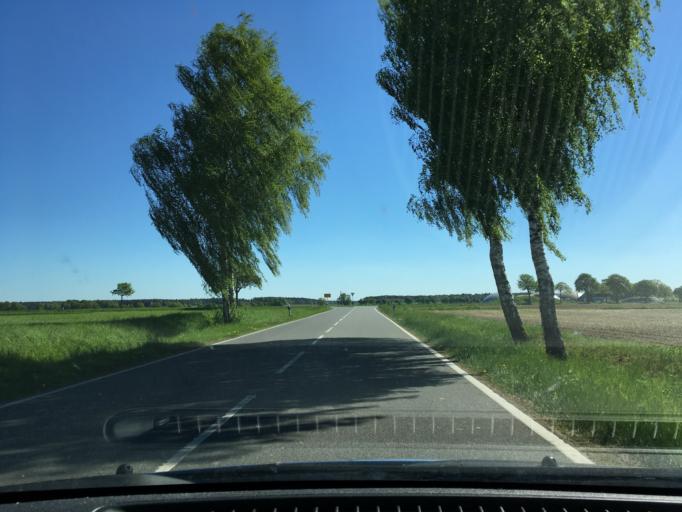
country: DE
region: Lower Saxony
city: Bergen
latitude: 52.8202
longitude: 10.0084
